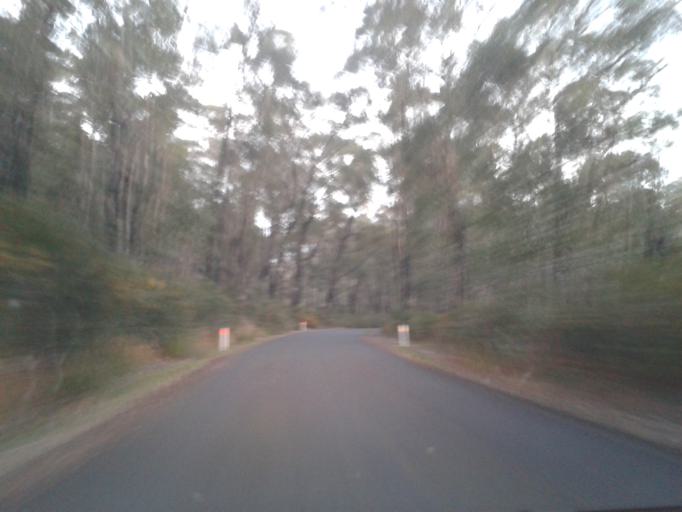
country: AU
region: Victoria
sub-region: Northern Grampians
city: Stawell
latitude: -37.1667
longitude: 142.4991
